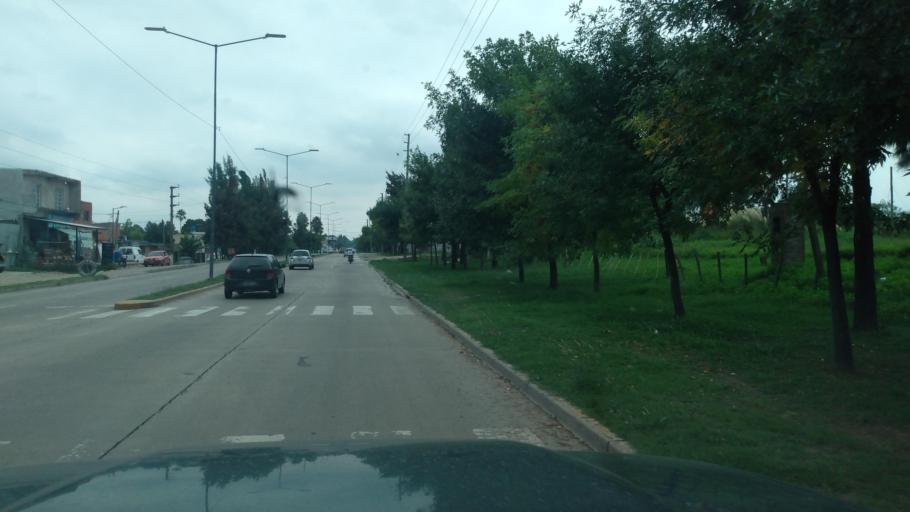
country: AR
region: Buenos Aires
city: Hurlingham
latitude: -34.5801
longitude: -58.6823
